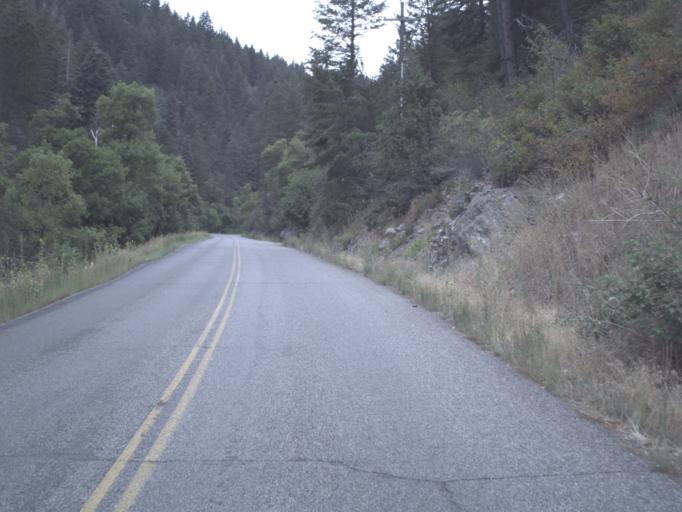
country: US
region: Utah
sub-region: Utah County
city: Orem
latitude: 40.3834
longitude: -111.5718
